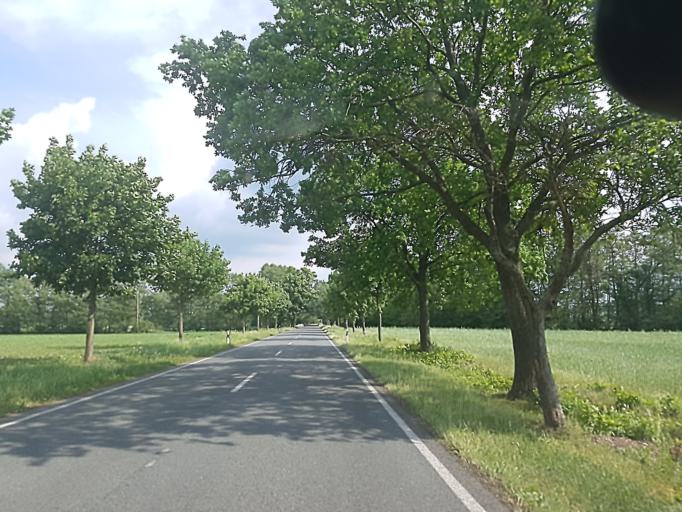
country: DE
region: Saxony-Anhalt
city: Lindau
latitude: 52.0180
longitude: 12.2283
